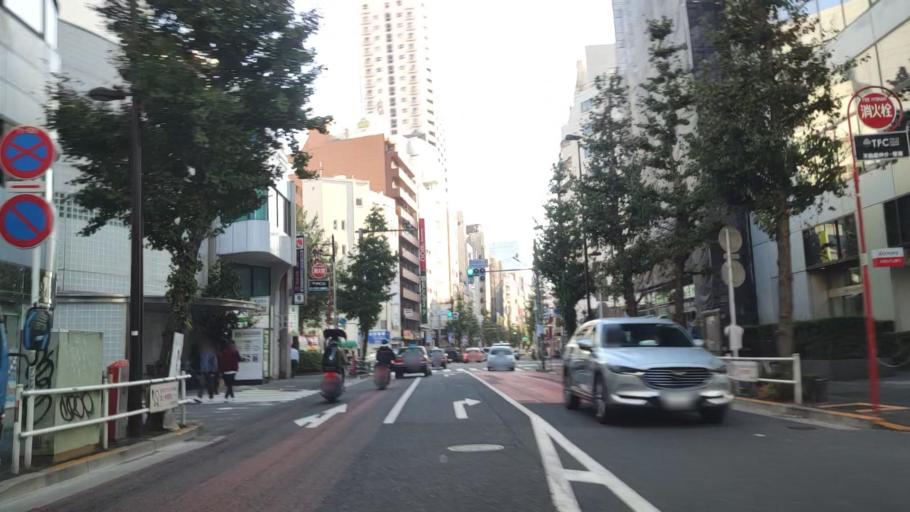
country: JP
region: Tokyo
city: Tokyo
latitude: 35.6985
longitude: 139.6970
